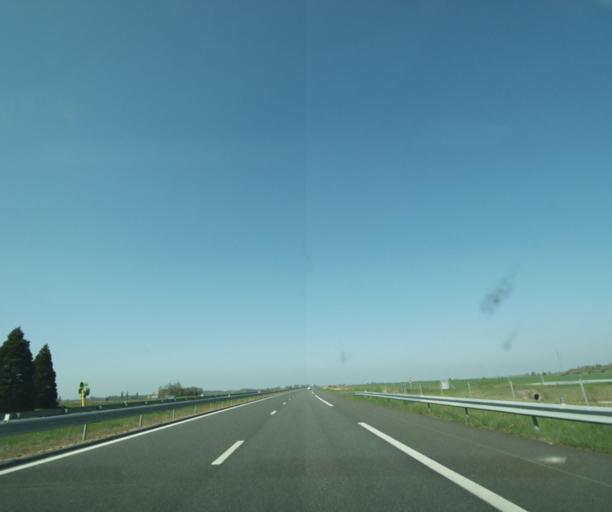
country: FR
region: Centre
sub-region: Departement du Loiret
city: Vimory
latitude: 47.9033
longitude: 2.6800
